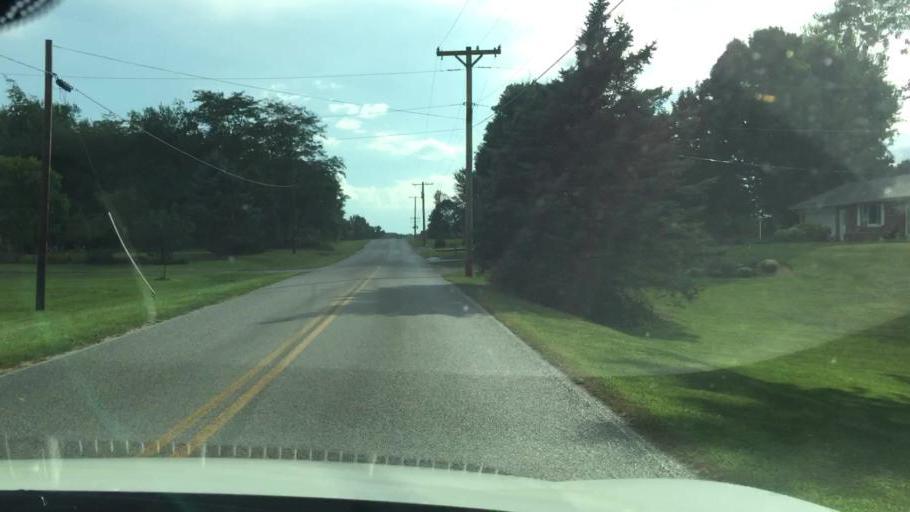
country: US
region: Ohio
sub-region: Champaign County
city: Mechanicsburg
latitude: 40.0734
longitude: -83.5749
